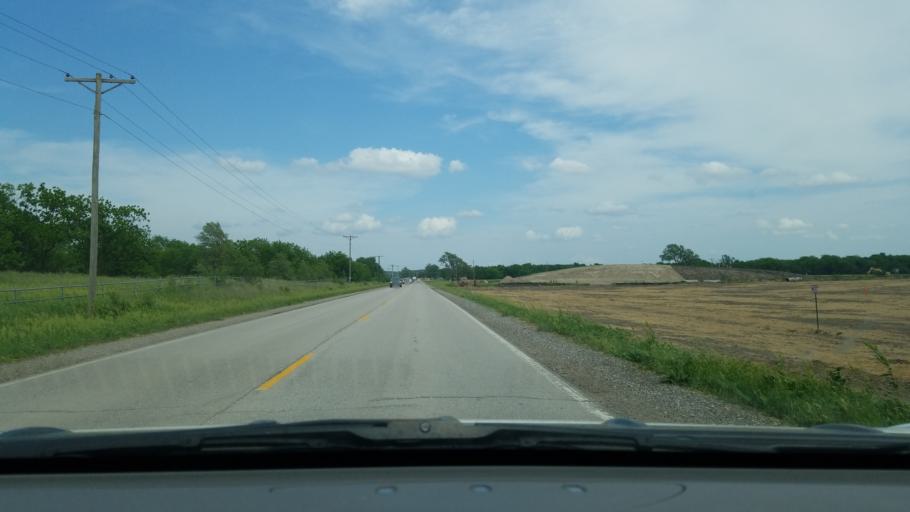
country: US
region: Nebraska
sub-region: Saunders County
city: Ashland
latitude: 41.0597
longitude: -96.3434
